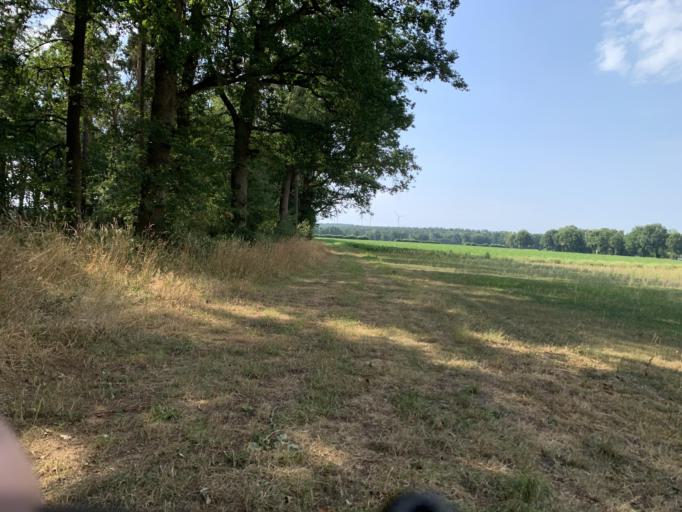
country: DE
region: Lower Saxony
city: Thomasburg
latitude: 53.2402
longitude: 10.6379
